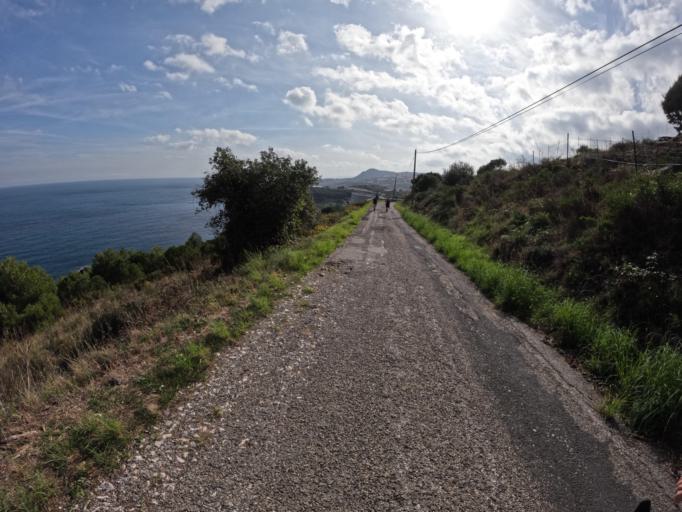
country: FR
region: Languedoc-Roussillon
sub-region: Departement des Pyrenees-Orientales
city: Cervera de la Marenda
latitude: 42.4624
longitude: 3.1585
